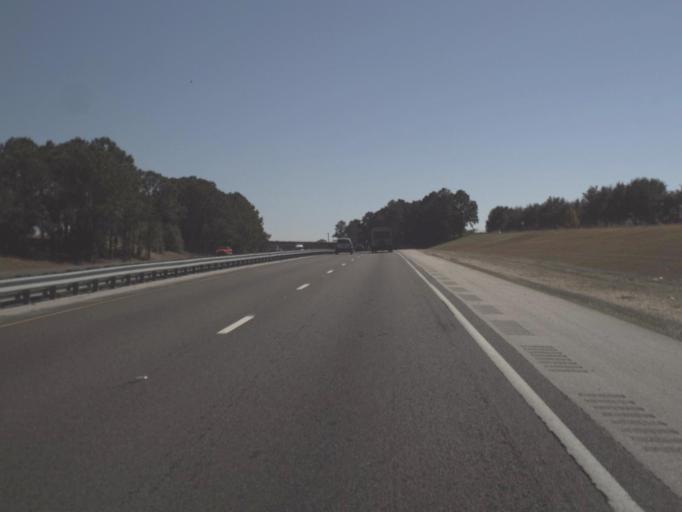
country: US
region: Florida
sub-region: Lake County
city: Montverde
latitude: 28.5633
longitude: -81.6856
